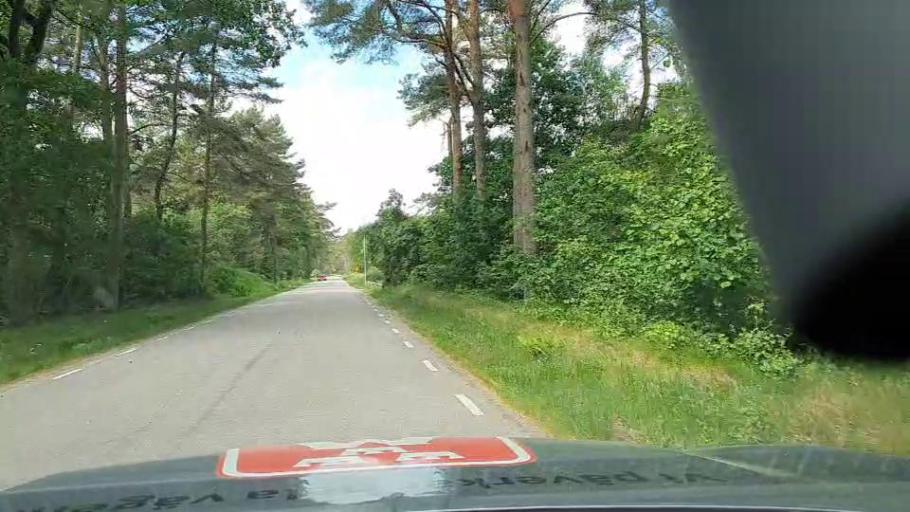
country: SE
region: Blekinge
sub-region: Karlshamns Kommun
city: Morrum
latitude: 56.0937
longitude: 14.6946
